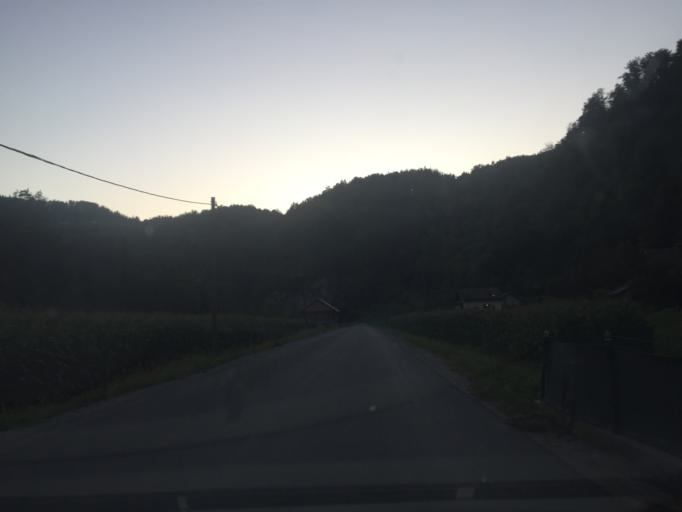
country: SI
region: Sostanj
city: Sostanj
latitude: 46.3707
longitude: 15.0221
